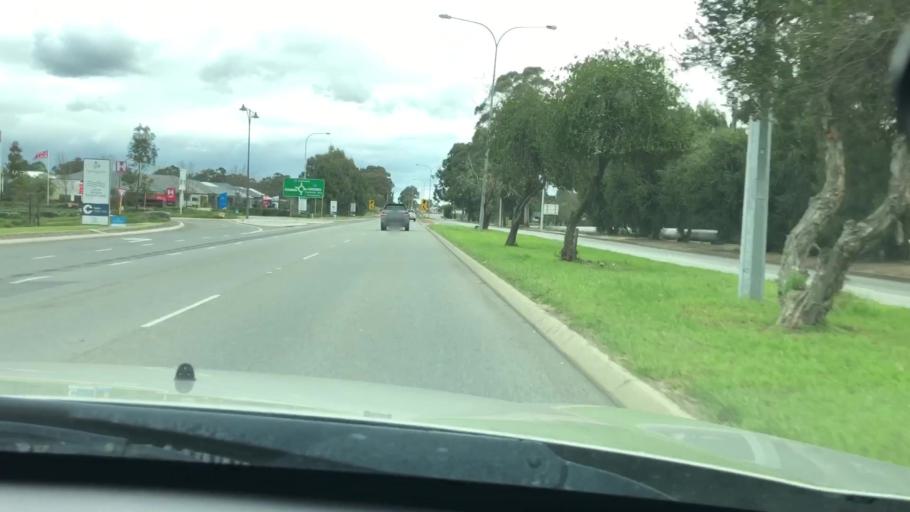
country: AU
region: Western Australia
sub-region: Armadale
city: Seville Grove
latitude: -32.1472
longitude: 115.9783
